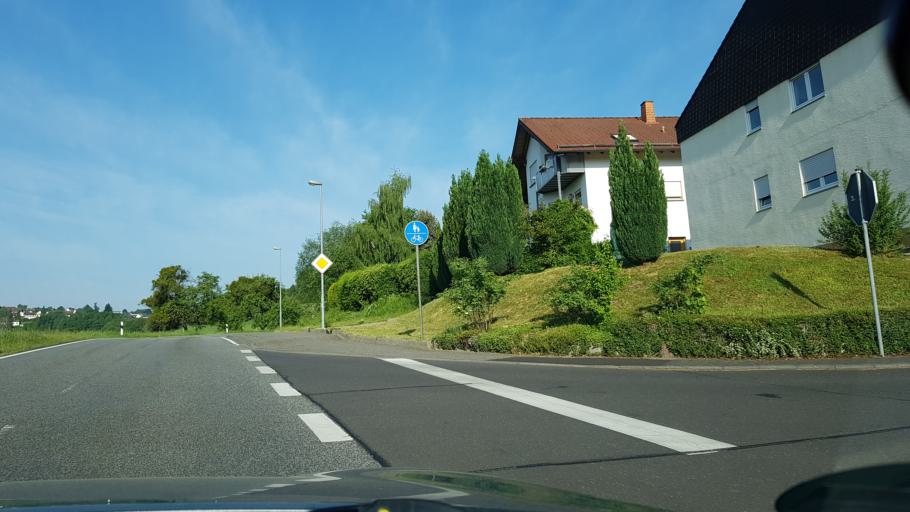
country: DE
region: Rheinland-Pfalz
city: Kadenbach
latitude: 50.3846
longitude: 7.7256
